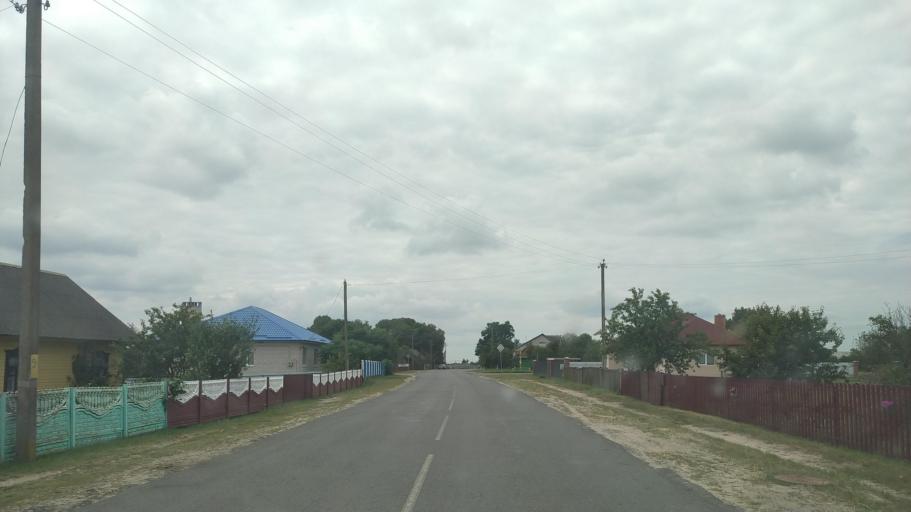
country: BY
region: Brest
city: Byaroza
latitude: 52.5422
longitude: 25.0767
